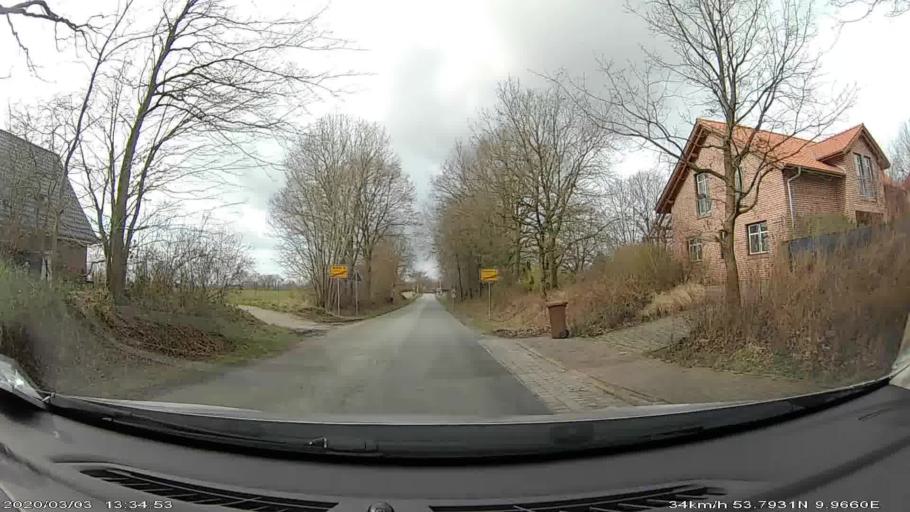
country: DE
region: Schleswig-Holstein
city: Henstedt-Ulzburg
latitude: 53.7934
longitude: 9.9650
